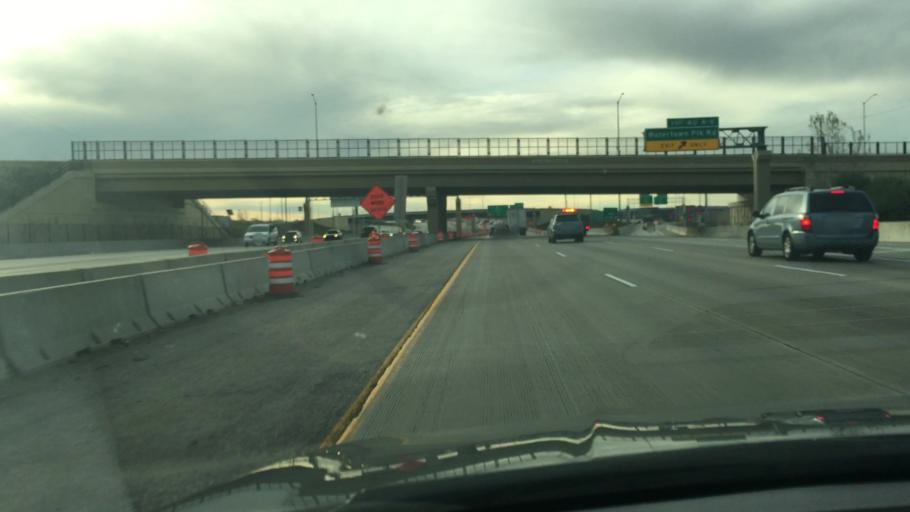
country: US
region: Wisconsin
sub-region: Milwaukee County
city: Wauwatosa
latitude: 43.0512
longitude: -88.0408
